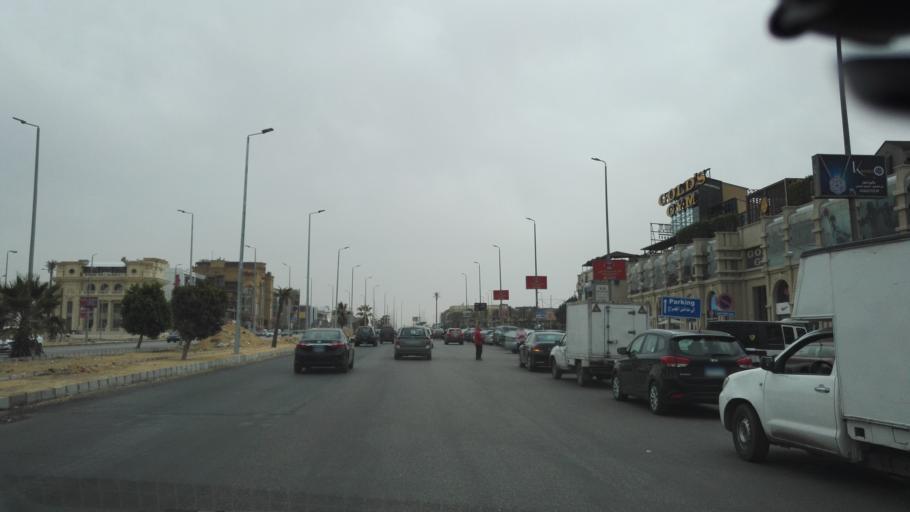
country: EG
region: Muhafazat al Qalyubiyah
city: Al Khankah
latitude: 30.0253
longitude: 31.4833
